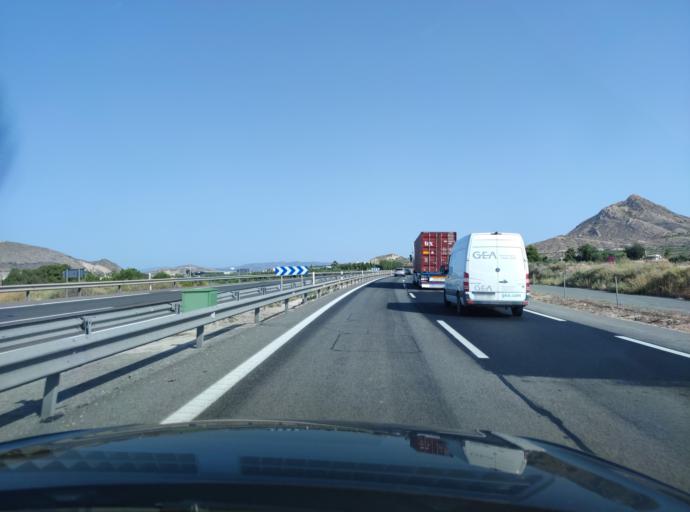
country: ES
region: Valencia
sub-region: Provincia de Alicante
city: Novelda
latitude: 38.4005
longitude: -0.7619
